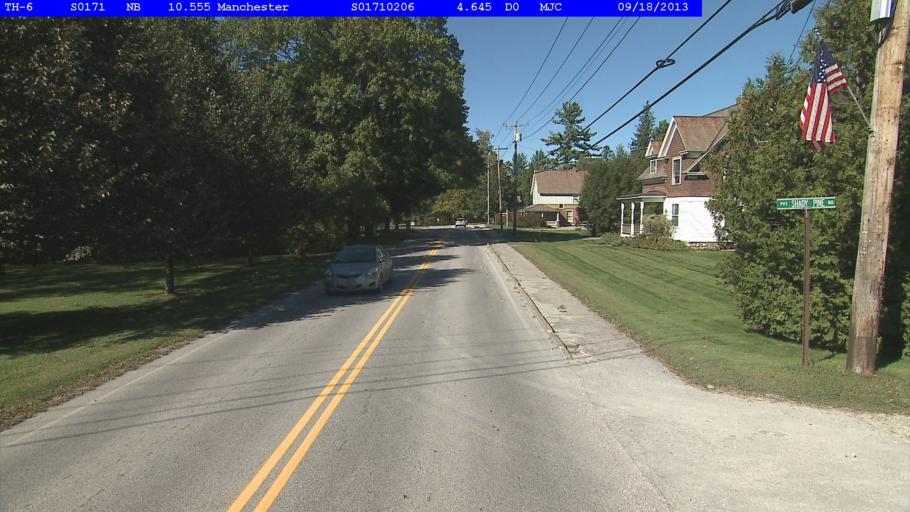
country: US
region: Vermont
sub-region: Bennington County
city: Manchester Center
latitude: 43.1696
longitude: -73.0486
